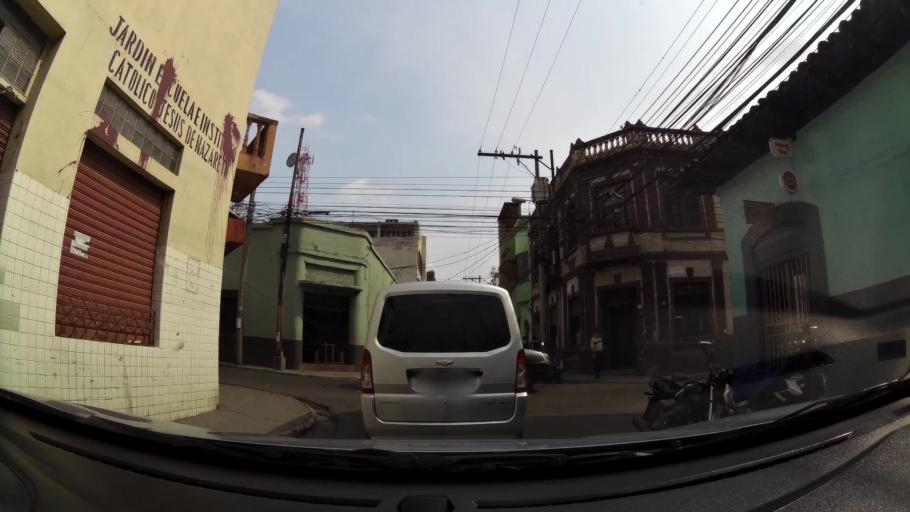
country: HN
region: Francisco Morazan
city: Tegucigalpa
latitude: 14.1080
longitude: -87.2075
